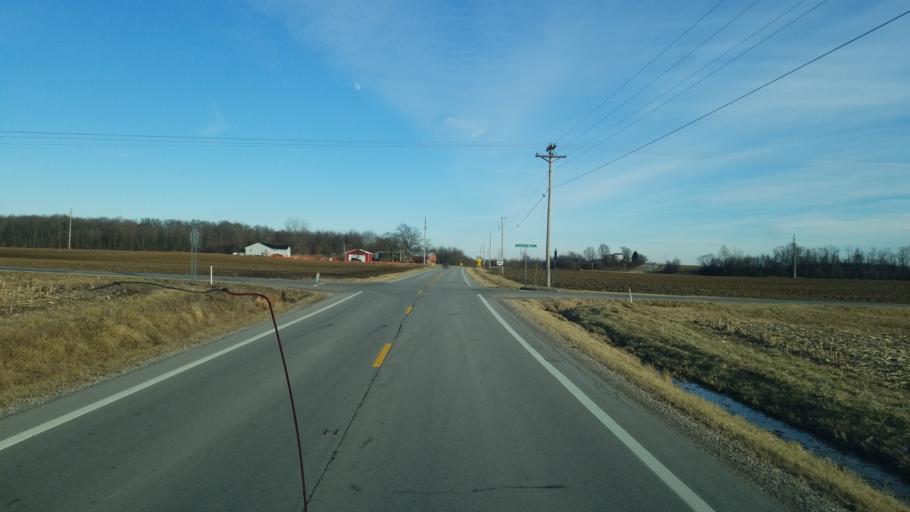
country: US
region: Ohio
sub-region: Huron County
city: Greenwich
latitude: 41.1029
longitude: -82.5381
